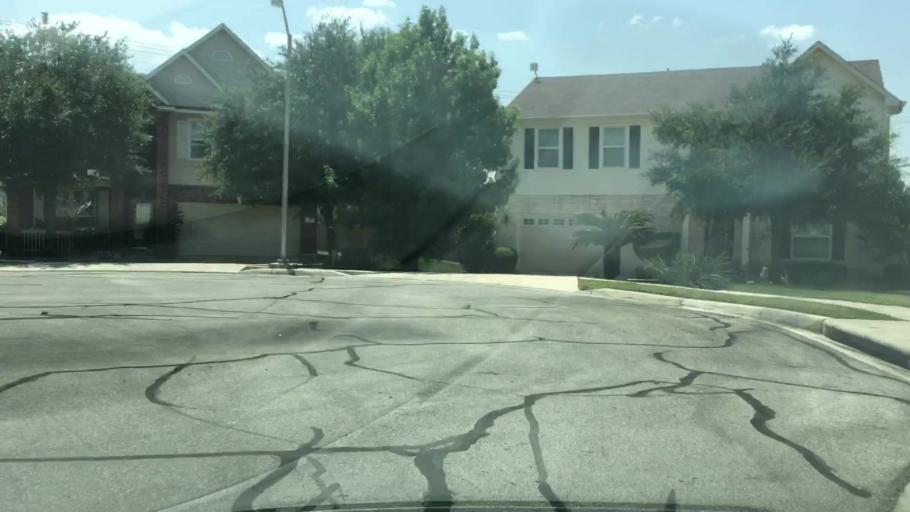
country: US
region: Texas
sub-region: Guadalupe County
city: Cibolo
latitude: 29.5821
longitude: -98.2504
